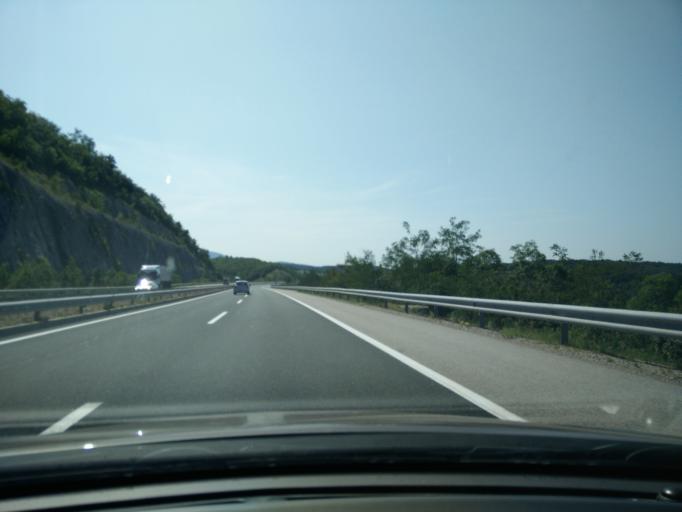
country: SI
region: Hrpelje-Kozina
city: Kozina
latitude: 45.5933
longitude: 13.9296
